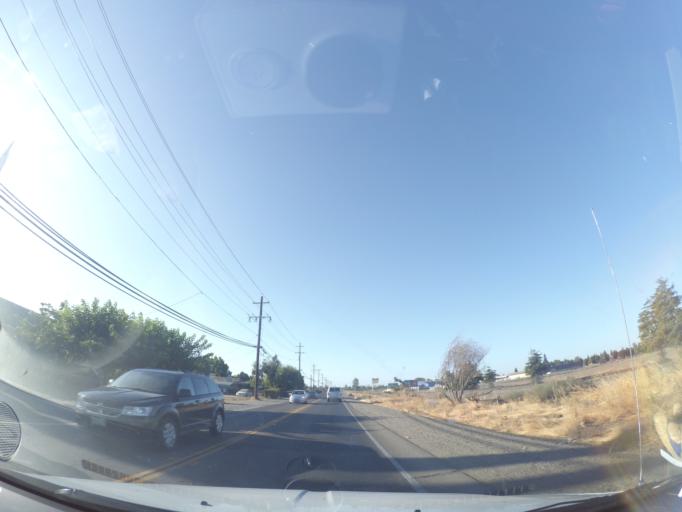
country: US
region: California
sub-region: Merced County
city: Merced
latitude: 37.3132
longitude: -120.5052
